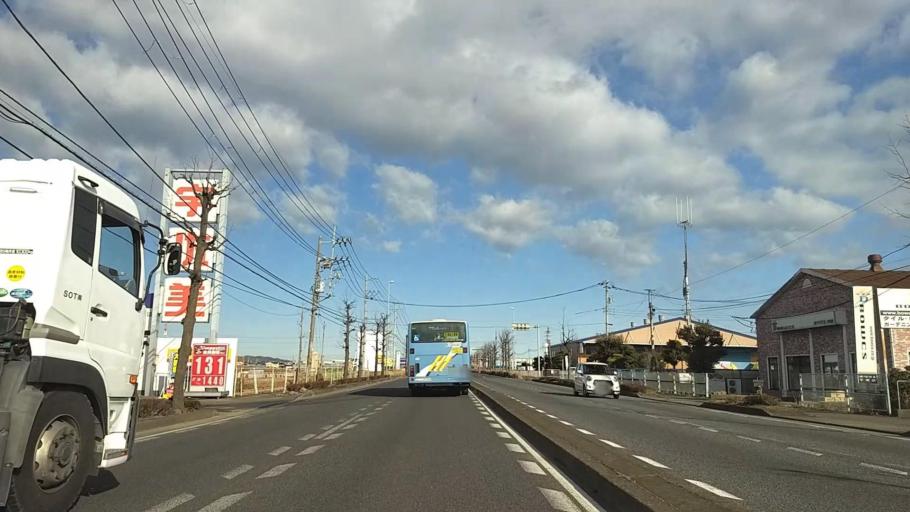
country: JP
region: Kanagawa
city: Atsugi
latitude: 35.3941
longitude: 139.3616
